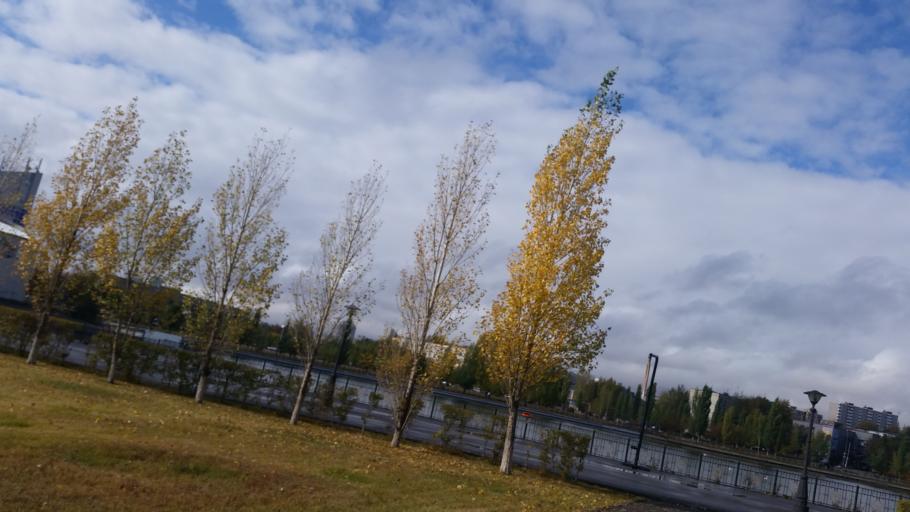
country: KZ
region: Astana Qalasy
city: Astana
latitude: 51.1542
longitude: 71.4573
